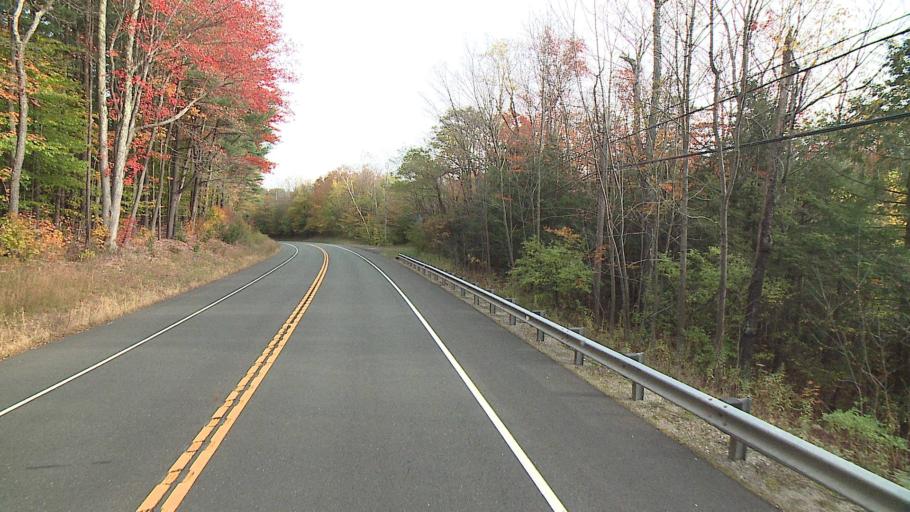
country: US
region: Connecticut
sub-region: Litchfield County
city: Winchester Center
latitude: 41.9647
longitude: -73.1362
